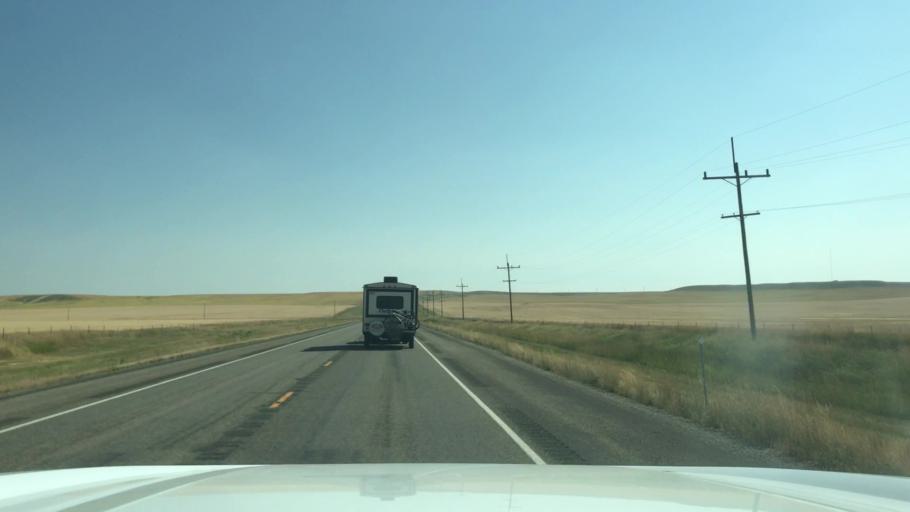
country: US
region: Montana
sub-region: Wheatland County
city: Harlowton
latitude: 46.4841
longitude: -109.7661
